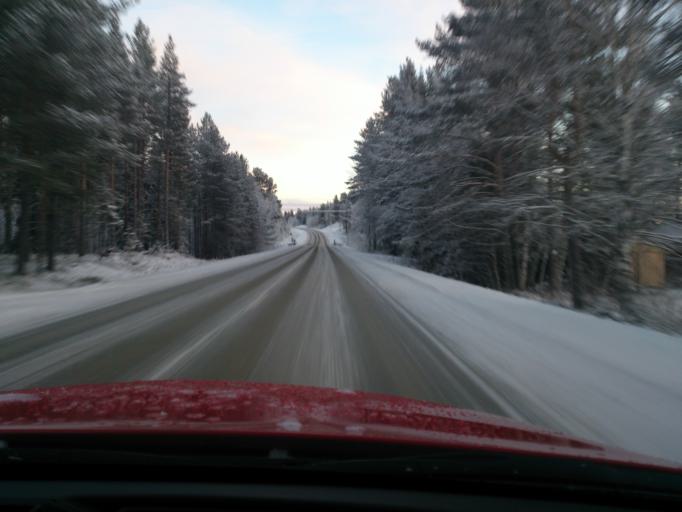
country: SE
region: Jaemtland
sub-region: Harjedalens Kommun
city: Sveg
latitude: 62.4126
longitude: 13.6383
